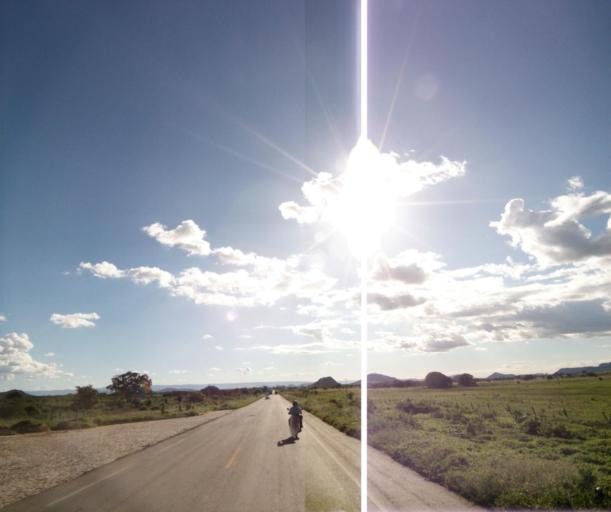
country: BR
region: Bahia
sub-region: Guanambi
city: Guanambi
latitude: -14.1577
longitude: -42.7083
